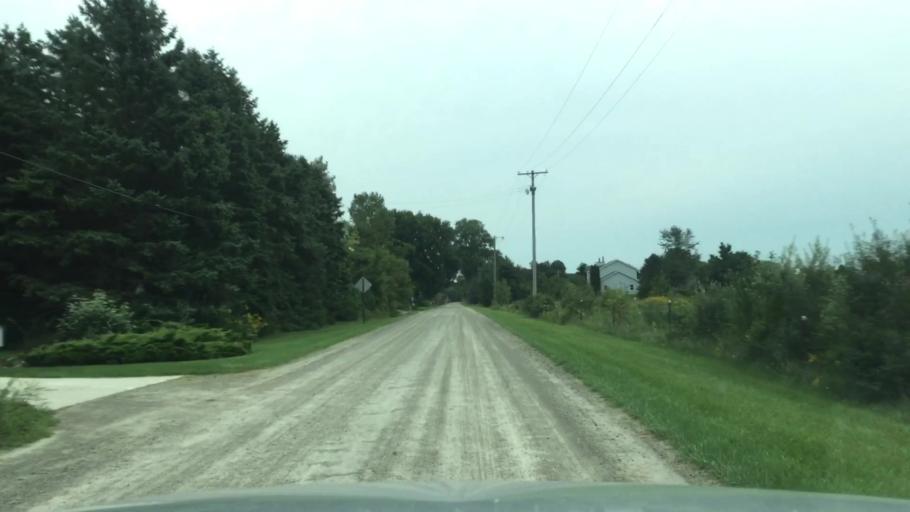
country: US
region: Michigan
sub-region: Washtenaw County
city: Milan
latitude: 42.0904
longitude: -83.7336
